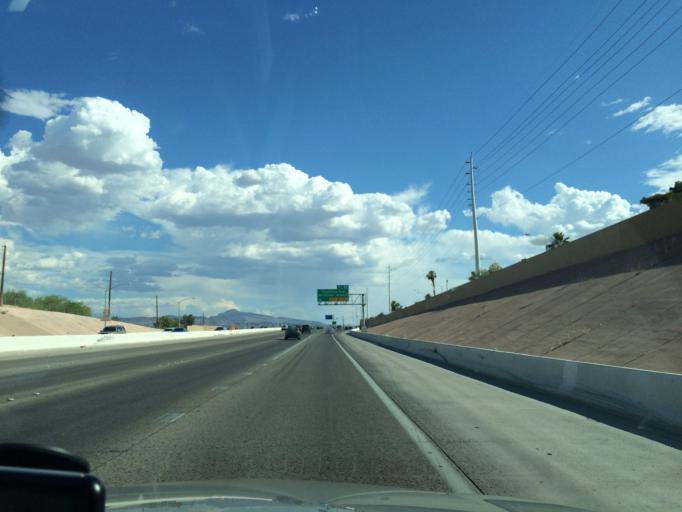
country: US
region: Nevada
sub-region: Clark County
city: Whitney
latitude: 36.1065
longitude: -115.0826
